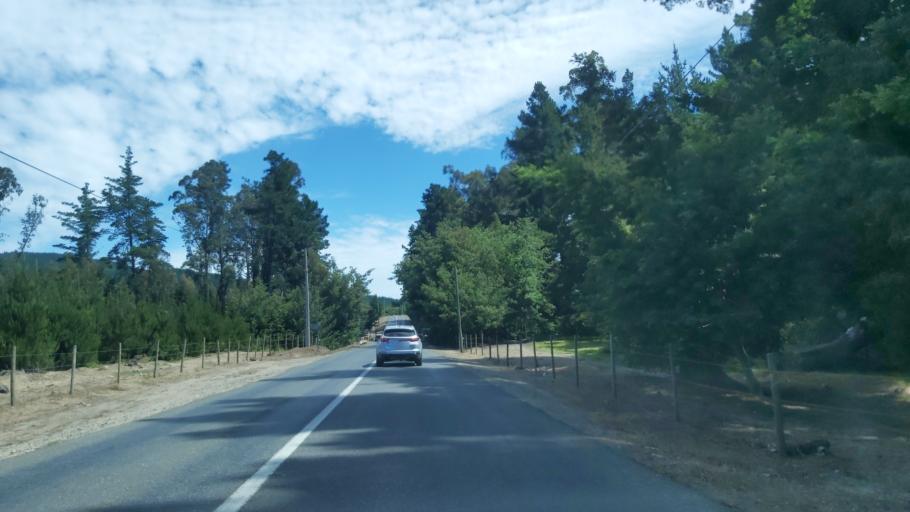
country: CL
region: Maule
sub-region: Provincia de Talca
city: Constitucion
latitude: -35.5139
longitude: -72.5286
